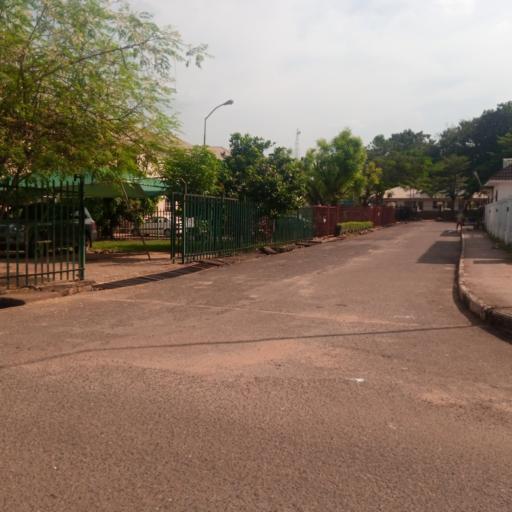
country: NG
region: Enugu
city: Enugu
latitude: 6.4482
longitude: 7.4883
